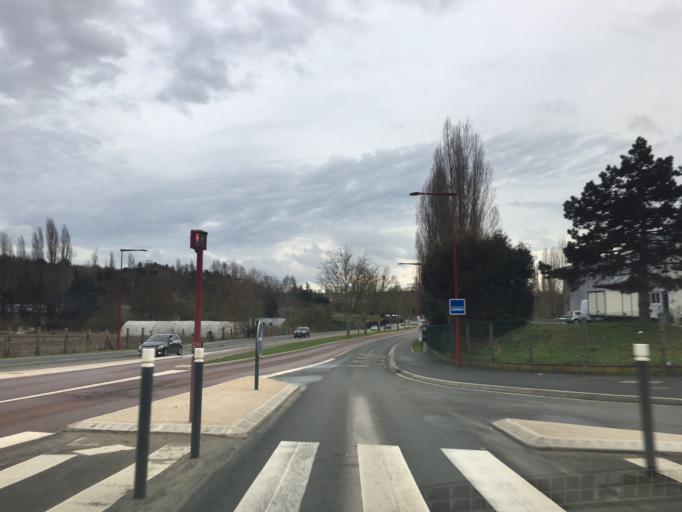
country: FR
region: Ile-de-France
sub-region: Departement du Val-d'Oise
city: Gonesse
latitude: 48.9886
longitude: 2.4587
